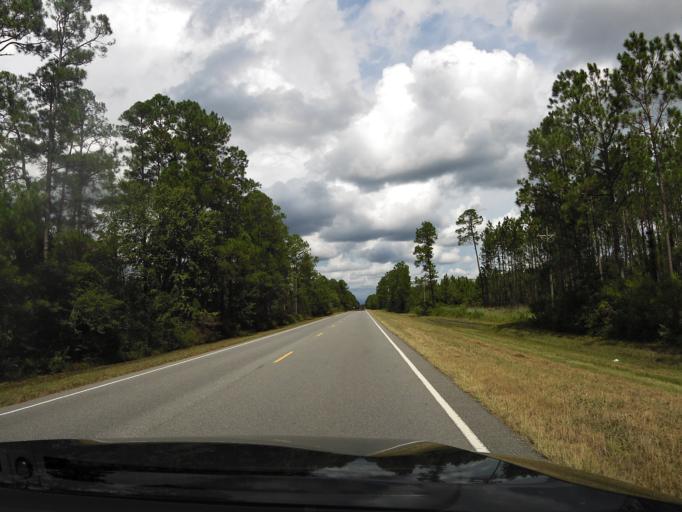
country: US
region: Georgia
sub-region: Brantley County
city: Nahunta
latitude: 31.1284
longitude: -81.9990
